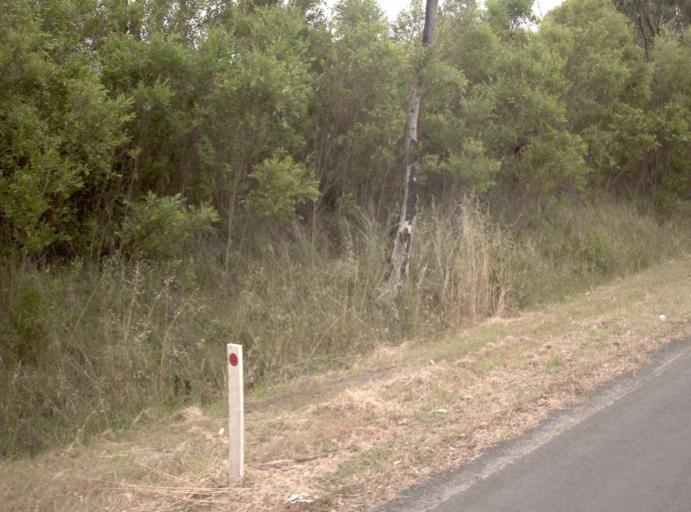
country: AU
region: Victoria
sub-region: Latrobe
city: Moe
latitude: -38.3039
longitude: 146.2792
